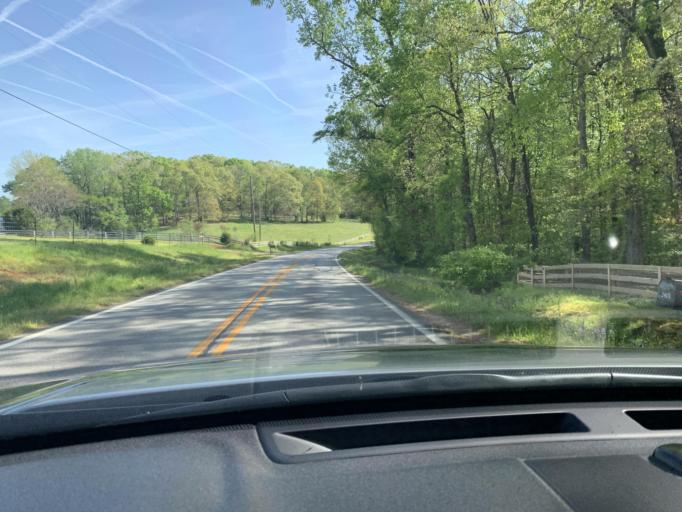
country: US
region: Georgia
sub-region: Oconee County
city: Watkinsville
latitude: 33.8036
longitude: -83.3182
